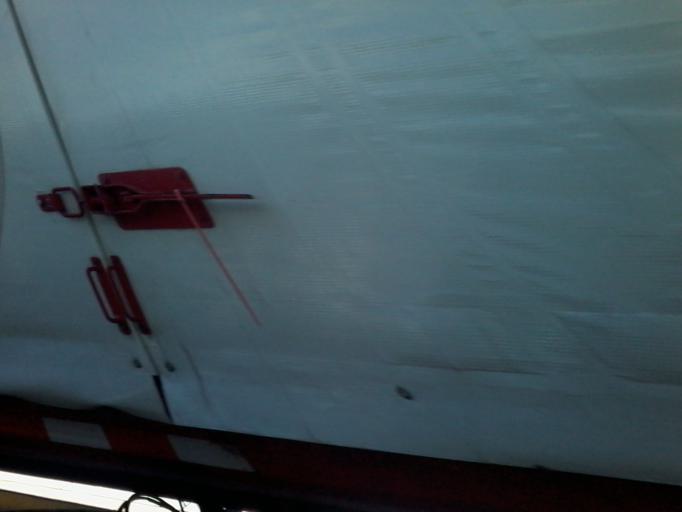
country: PE
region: Ayacucho
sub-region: Provincia de Huamanga
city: Ayacucho
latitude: -13.1535
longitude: -74.2070
